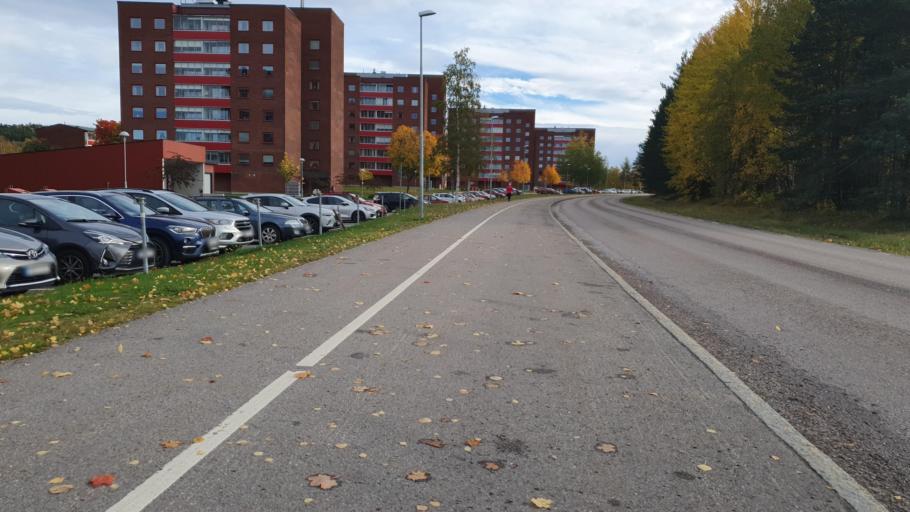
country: SE
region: Vaesternorrland
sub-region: Sundsvalls Kommun
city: Sundsvall
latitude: 62.4046
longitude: 17.2478
